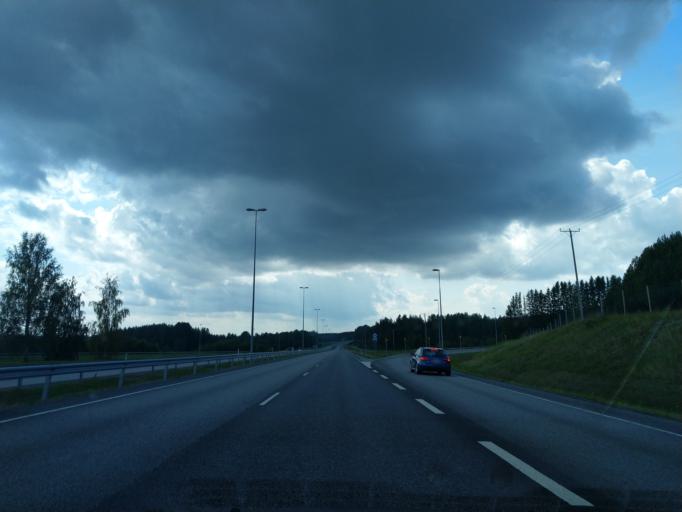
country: FI
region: South Karelia
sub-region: Imatra
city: Imatra
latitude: 61.1722
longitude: 28.6986
